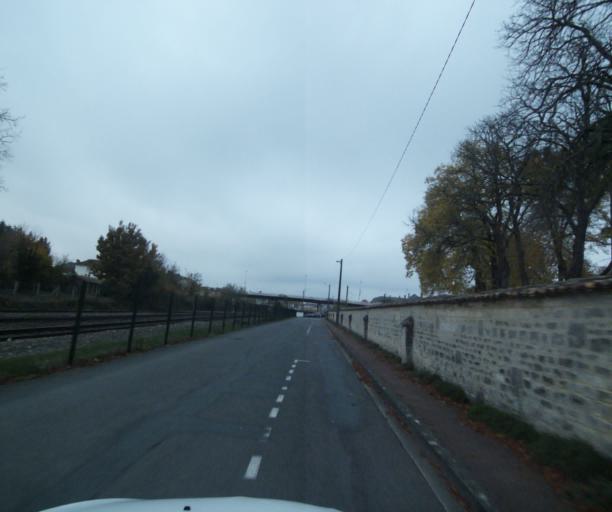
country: FR
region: Poitou-Charentes
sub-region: Departement de la Charente-Maritime
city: Saintes
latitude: 45.7442
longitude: -0.6182
